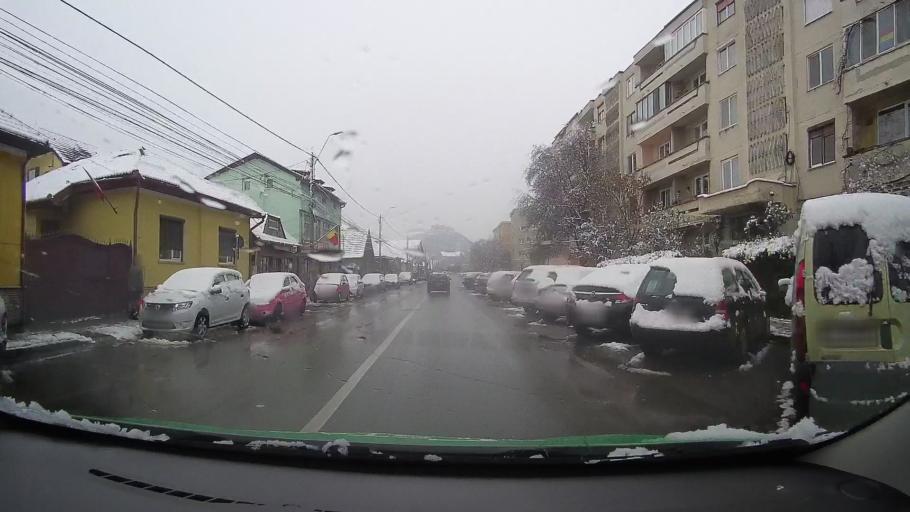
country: RO
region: Hunedoara
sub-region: Municipiul Deva
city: Deva
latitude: 45.8710
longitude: 22.9038
